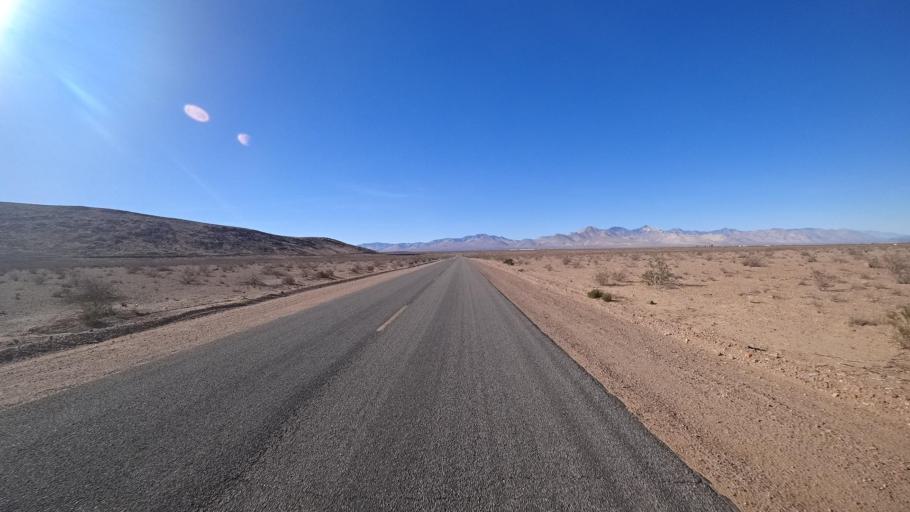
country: US
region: California
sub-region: Kern County
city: China Lake Acres
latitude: 35.5583
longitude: -117.7642
